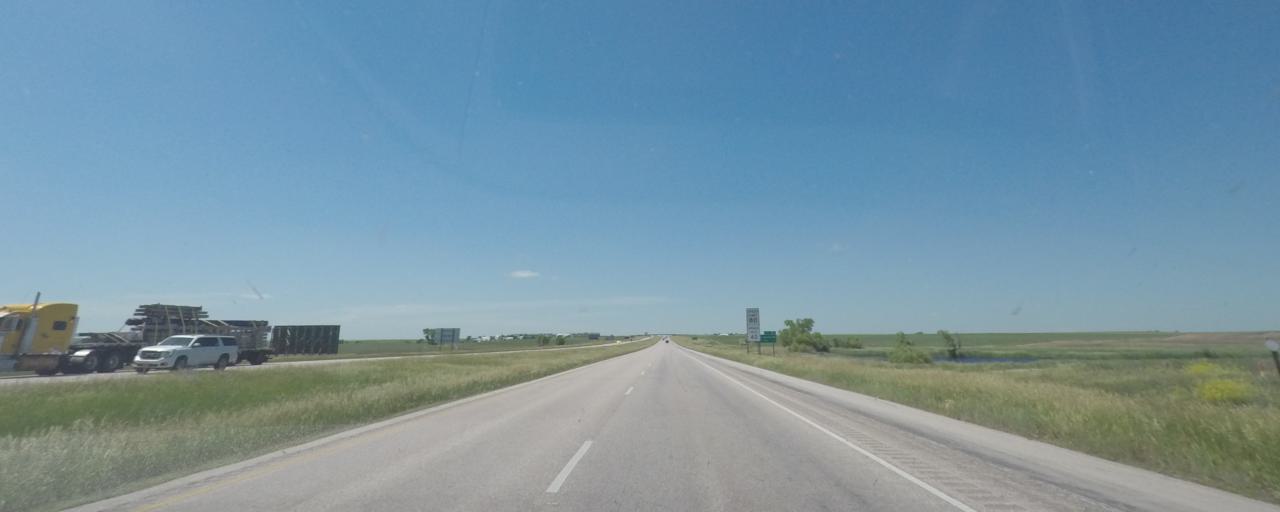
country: US
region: South Dakota
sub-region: Haakon County
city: Philip
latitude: 44.0002
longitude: -102.2665
